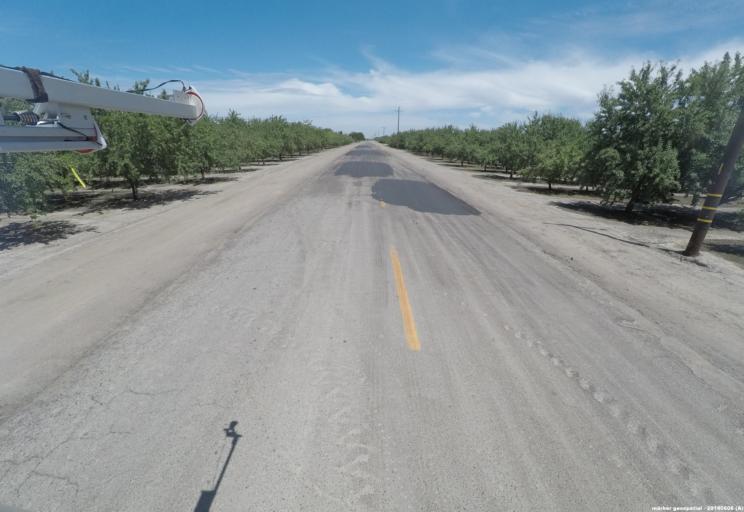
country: US
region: California
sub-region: Fresno County
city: Firebaugh
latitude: 36.8675
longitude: -120.3998
